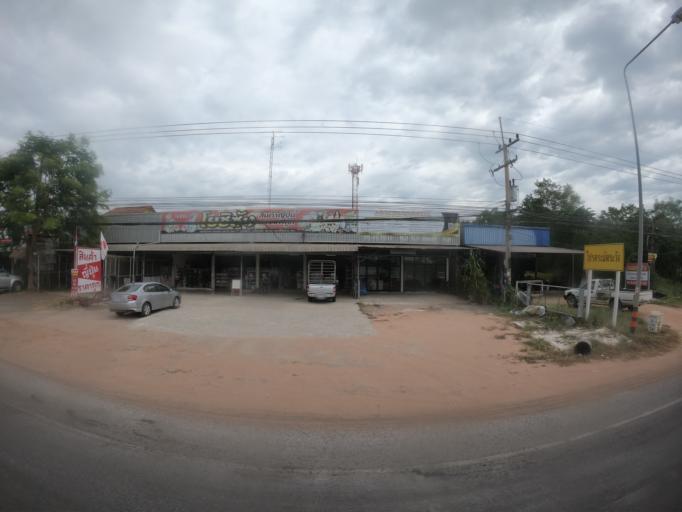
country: TH
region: Maha Sarakham
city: Maha Sarakham
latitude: 16.2063
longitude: 103.2864
